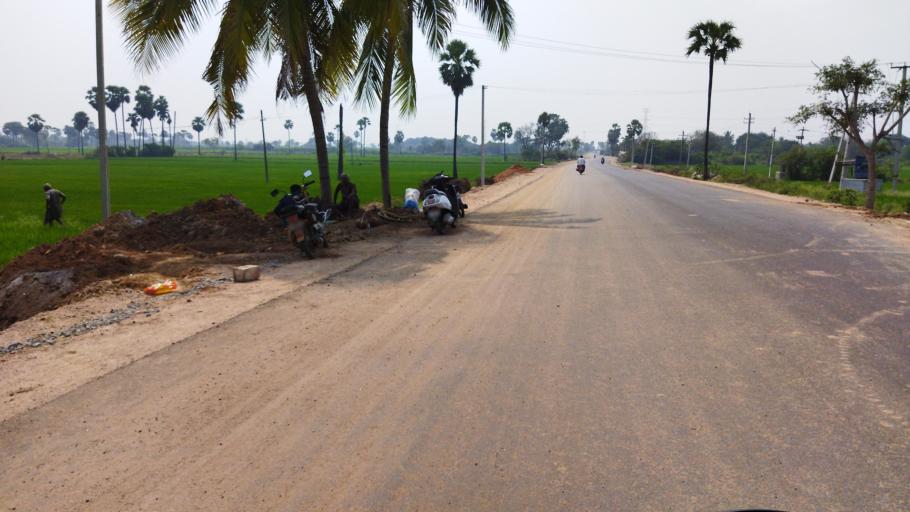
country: IN
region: Telangana
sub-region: Nalgonda
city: Nalgonda
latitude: 17.1203
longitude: 79.3649
